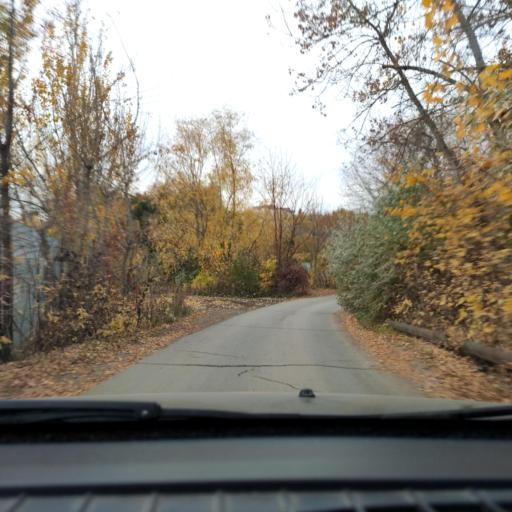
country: RU
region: Samara
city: Tol'yatti
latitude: 53.4978
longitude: 49.2626
